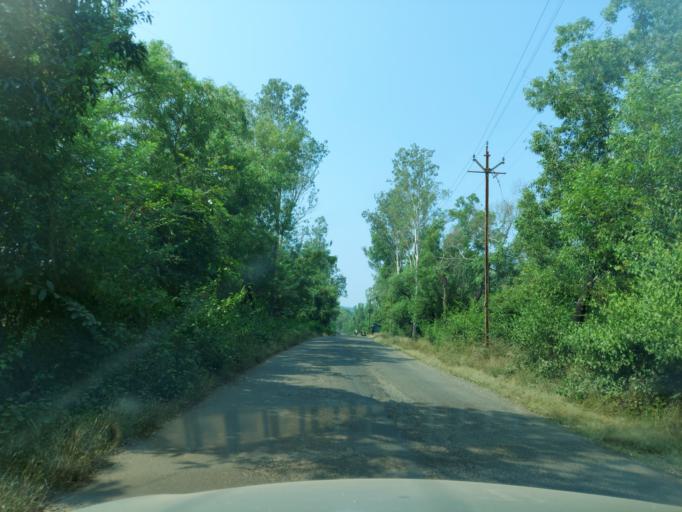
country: IN
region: Maharashtra
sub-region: Sindhudurg
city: Kudal
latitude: 15.9670
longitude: 73.5875
